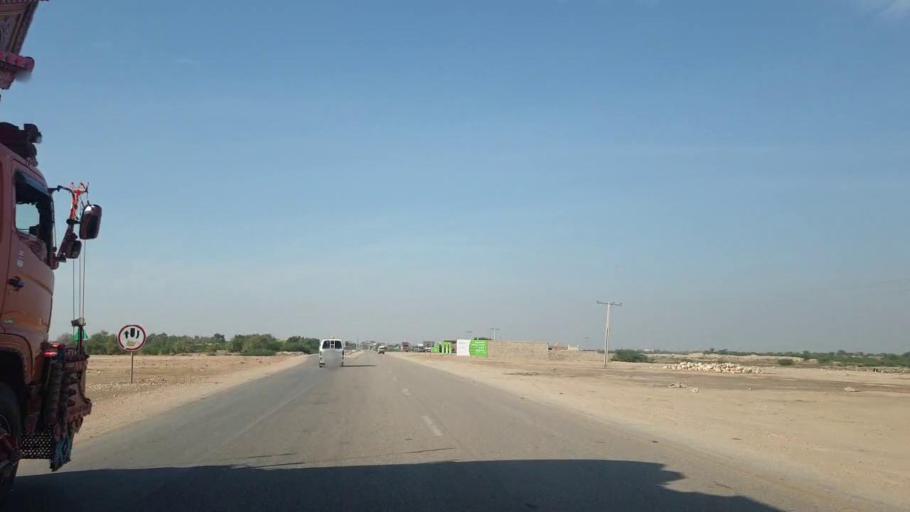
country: PK
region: Sindh
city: Sehwan
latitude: 26.3890
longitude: 67.8690
